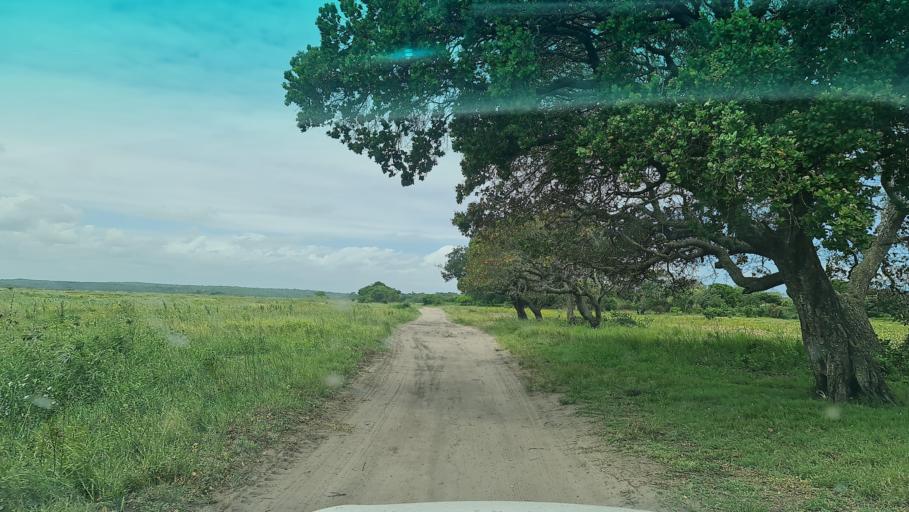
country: MZ
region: Maputo
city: Manhica
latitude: -25.5275
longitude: 32.8523
